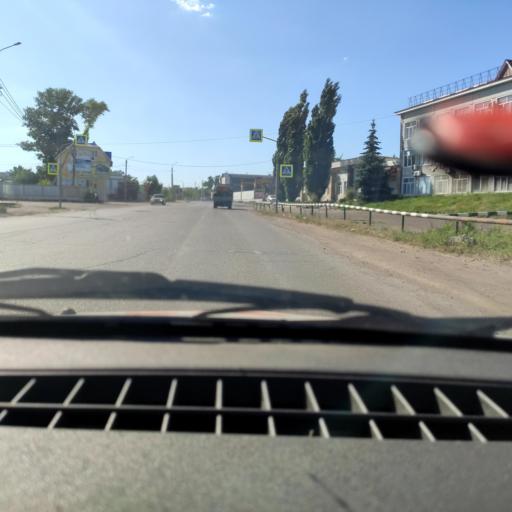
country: RU
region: Bashkortostan
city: Sterlitamak
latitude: 53.6514
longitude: 55.9758
